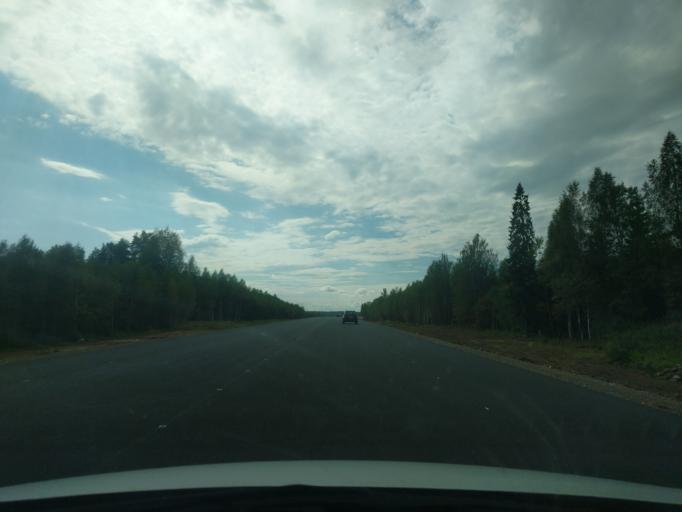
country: RU
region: Kostroma
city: Sudislavl'
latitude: 57.8164
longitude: 41.4798
